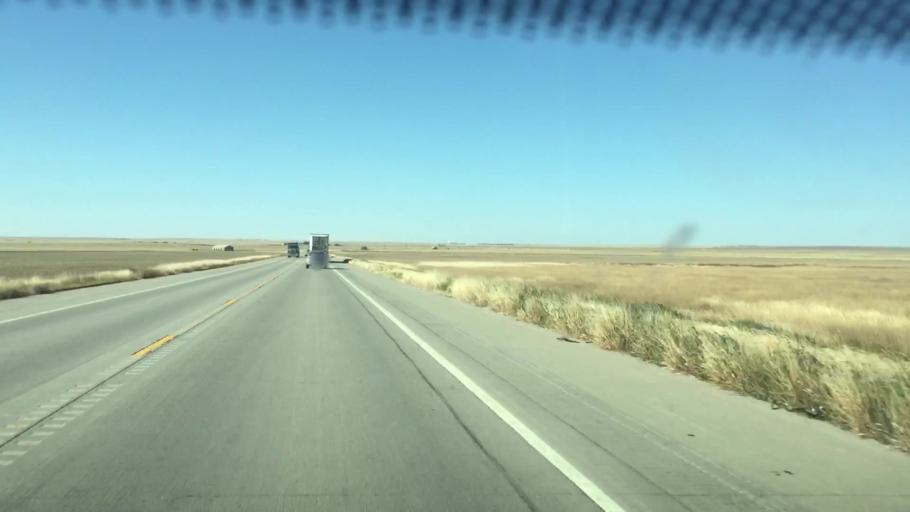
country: US
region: Colorado
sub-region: Kiowa County
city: Eads
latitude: 38.3656
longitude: -102.7235
